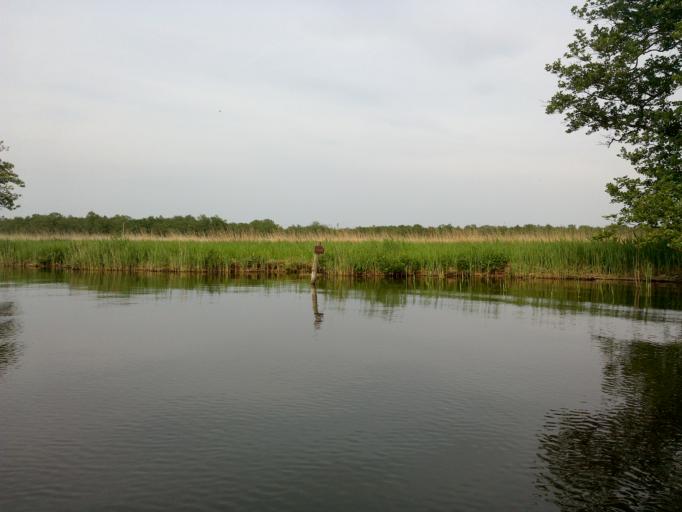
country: NL
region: South Holland
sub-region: Gemeente Nieuwkoop
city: Nieuwkoop
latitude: 52.1478
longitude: 4.7994
